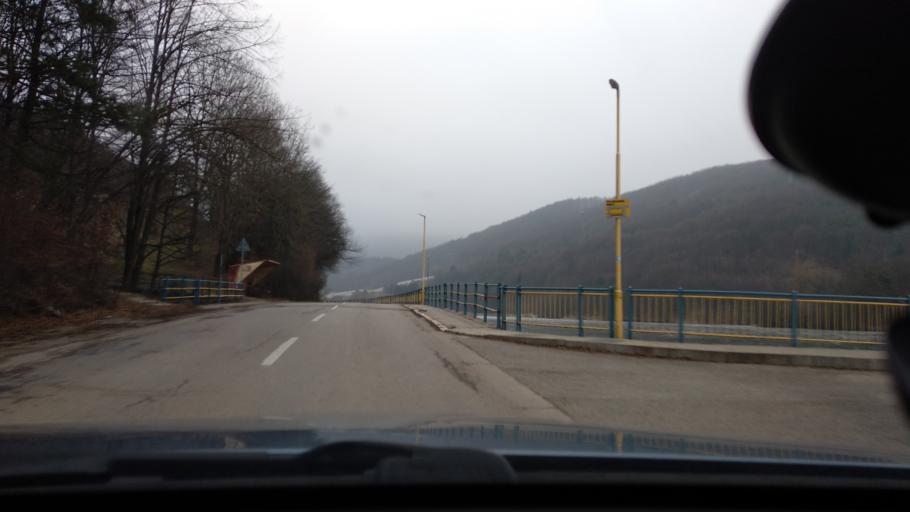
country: SK
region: Nitriansky
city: Trencianske Teplice
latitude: 48.9003
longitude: 18.1977
